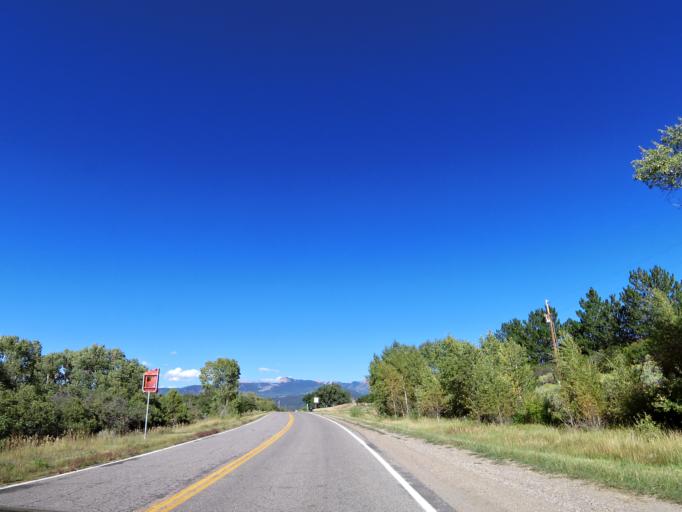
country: US
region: Colorado
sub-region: Montezuma County
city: Mancos
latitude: 37.3446
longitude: -108.2813
